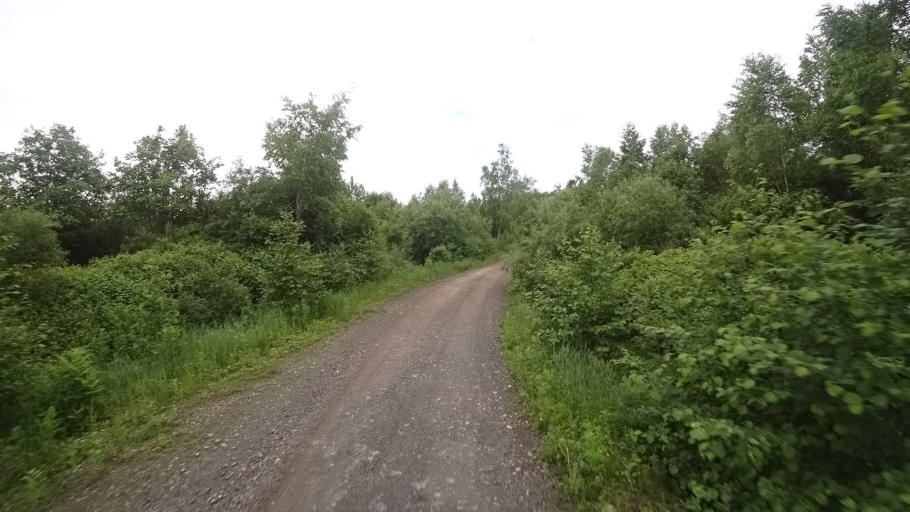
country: RU
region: Khabarovsk Krai
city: Amursk
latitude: 49.9119
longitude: 136.1582
